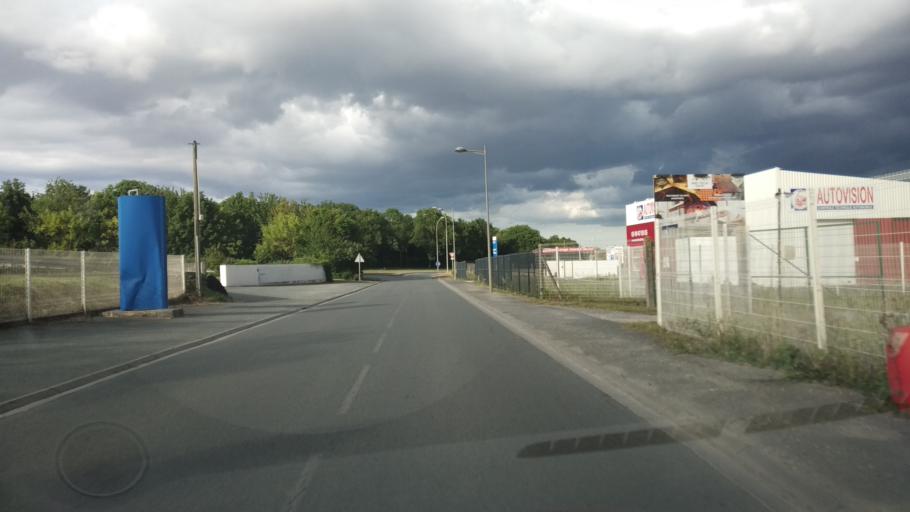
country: FR
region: Poitou-Charentes
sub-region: Departement de la Vienne
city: Migne-Auxances
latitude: 46.6162
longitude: 0.3118
